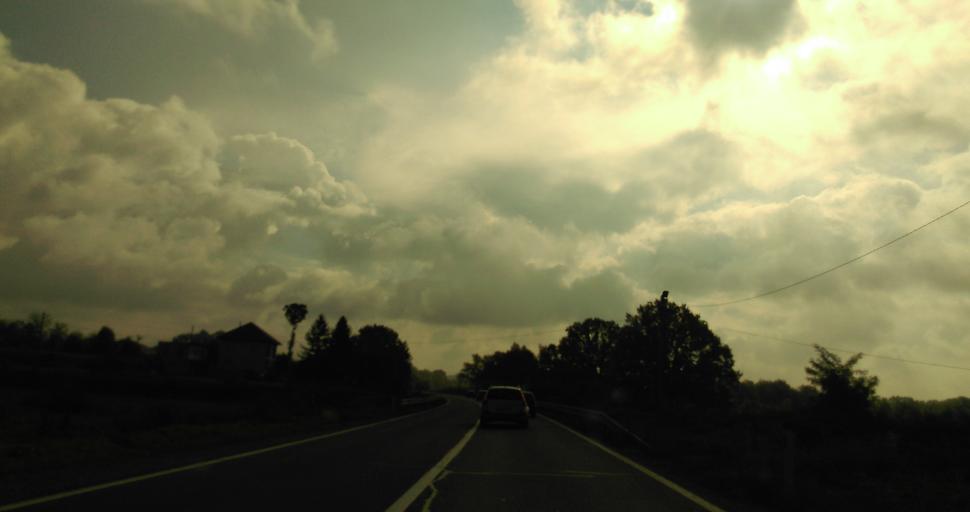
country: RS
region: Central Serbia
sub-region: Belgrade
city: Lazarevac
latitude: 44.3092
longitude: 20.2461
